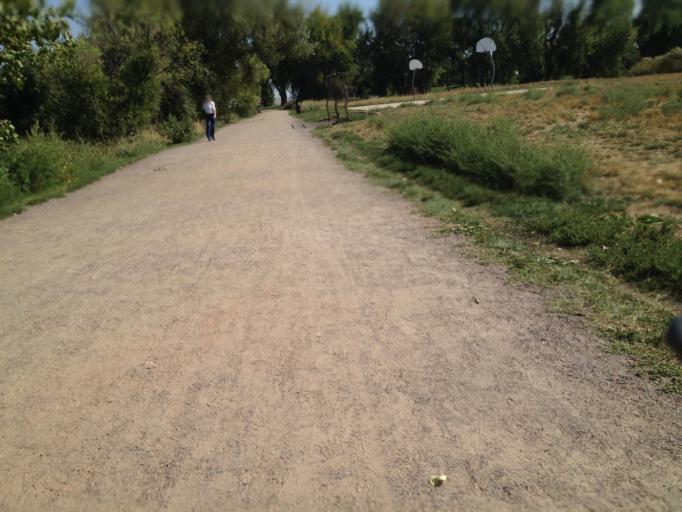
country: US
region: Colorado
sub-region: Boulder County
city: Louisville
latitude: 39.9941
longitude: -105.1160
